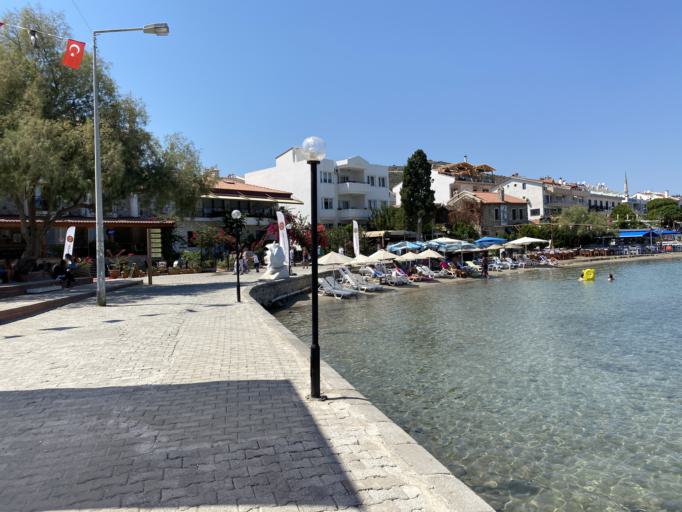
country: TR
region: Mugla
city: Datca
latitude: 36.7237
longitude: 27.6871
